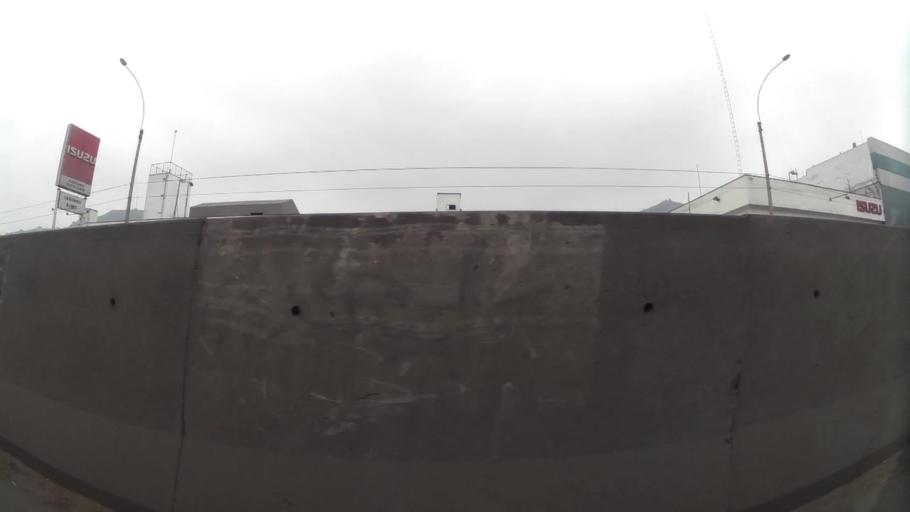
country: PE
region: Lima
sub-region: Lima
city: San Luis
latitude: -12.0641
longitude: -76.9924
